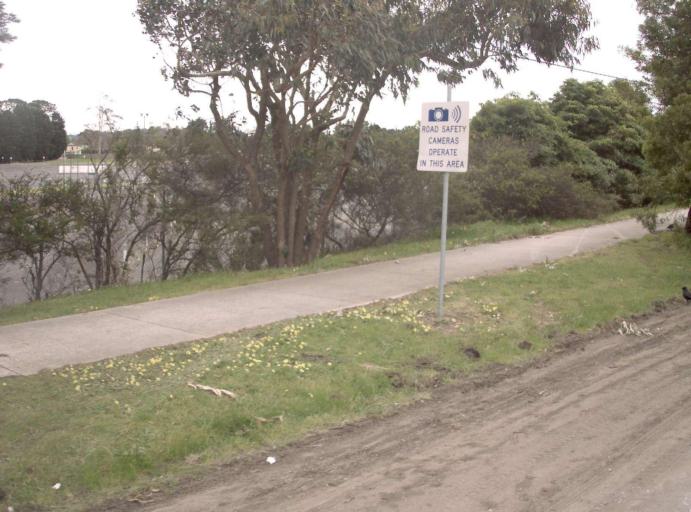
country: AU
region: Victoria
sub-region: Knox
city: Wantirna
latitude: -37.8508
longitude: 145.2241
